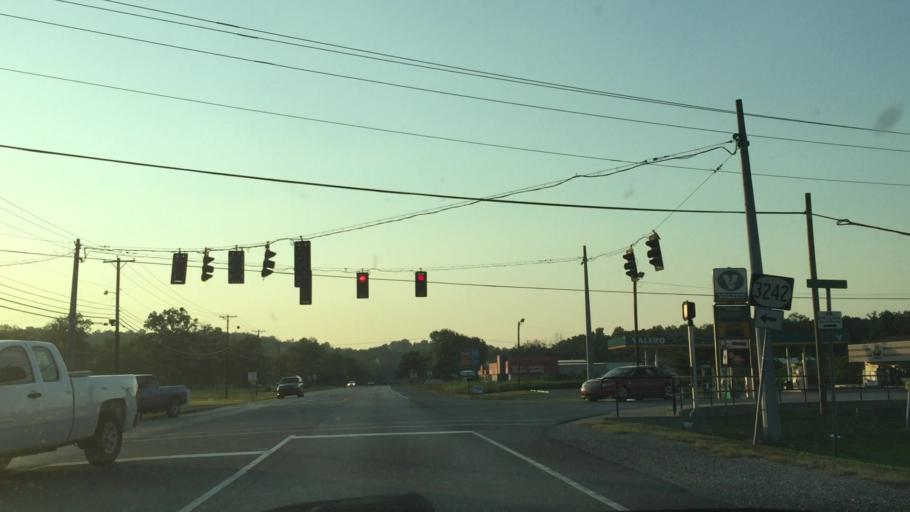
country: US
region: Kentucky
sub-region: Carroll County
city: Carrollton
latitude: 38.6638
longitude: -85.1411
